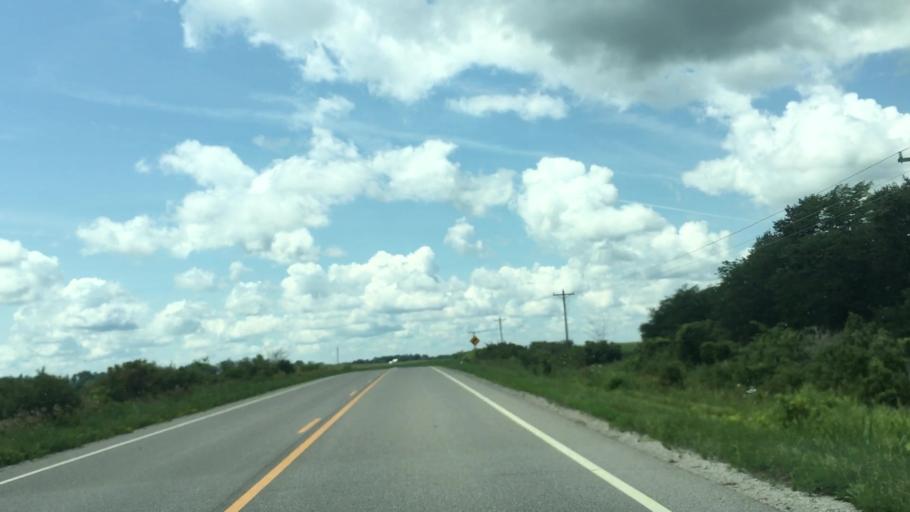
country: US
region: Iowa
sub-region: Johnson County
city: Solon
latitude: 41.8335
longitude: -91.4377
